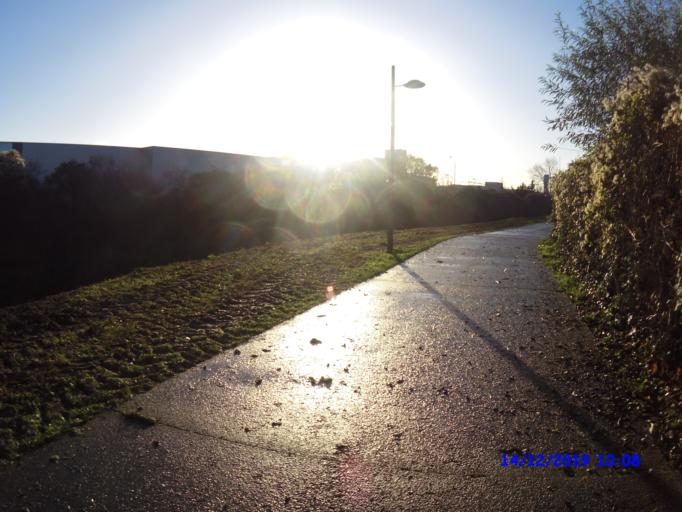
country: BE
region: Flanders
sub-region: Provincie Vlaams-Brabant
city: Drogenbos
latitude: 50.8168
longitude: 4.3032
